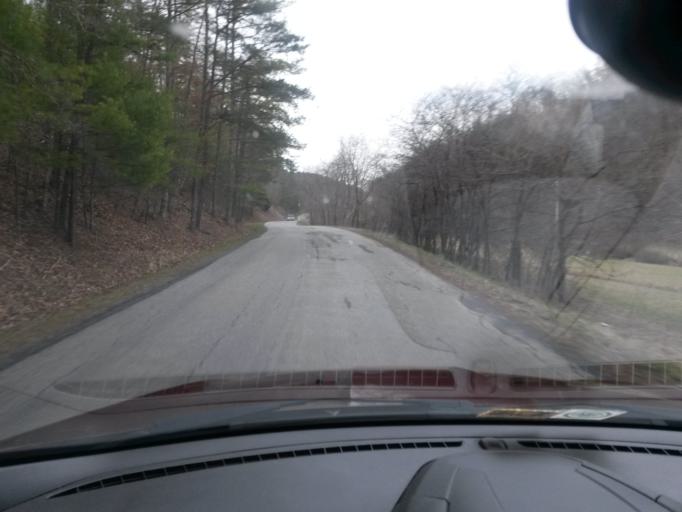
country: US
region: Virginia
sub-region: Bath County
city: Warm Springs
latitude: 38.0262
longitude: -79.8611
